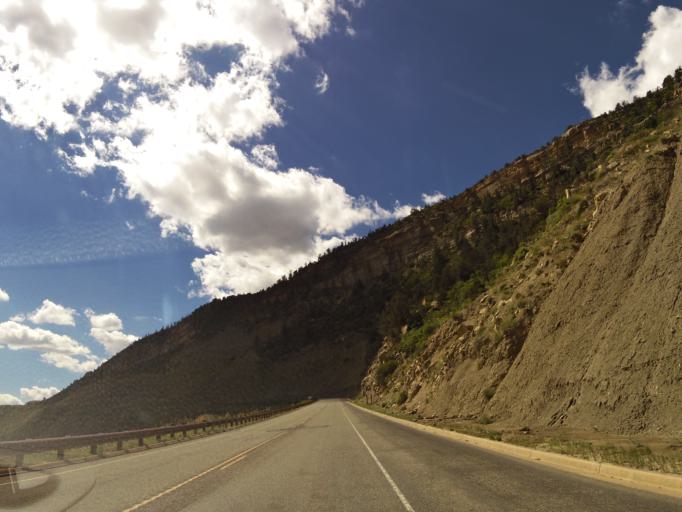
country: US
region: Colorado
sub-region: Montezuma County
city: Mancos
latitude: 37.3136
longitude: -108.4154
